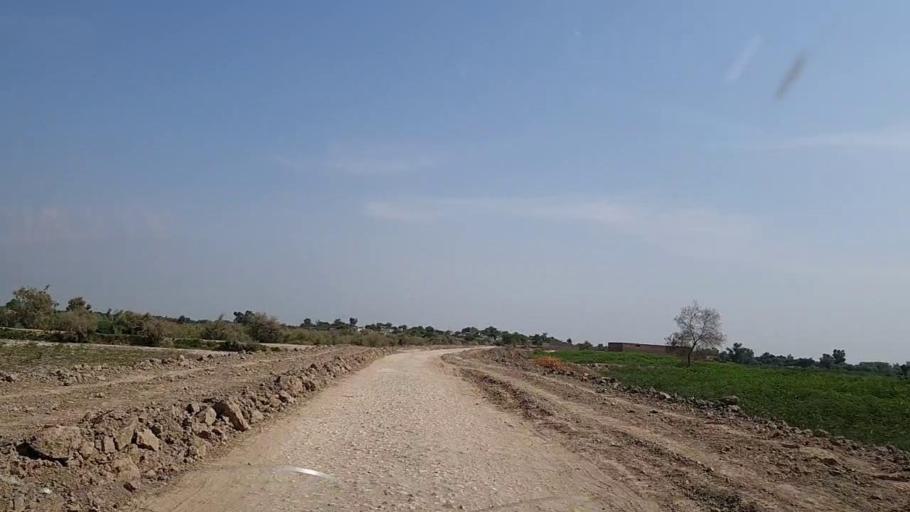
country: PK
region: Sindh
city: Khanpur
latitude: 27.7544
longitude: 69.3367
